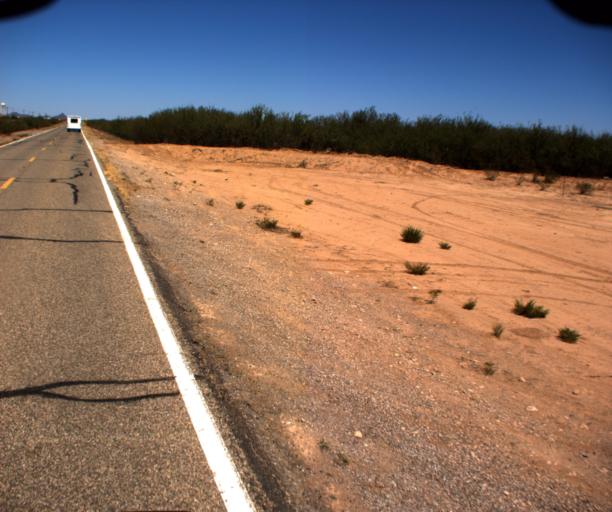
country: US
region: Arizona
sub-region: Pima County
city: Ajo
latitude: 32.1877
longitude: -112.3900
